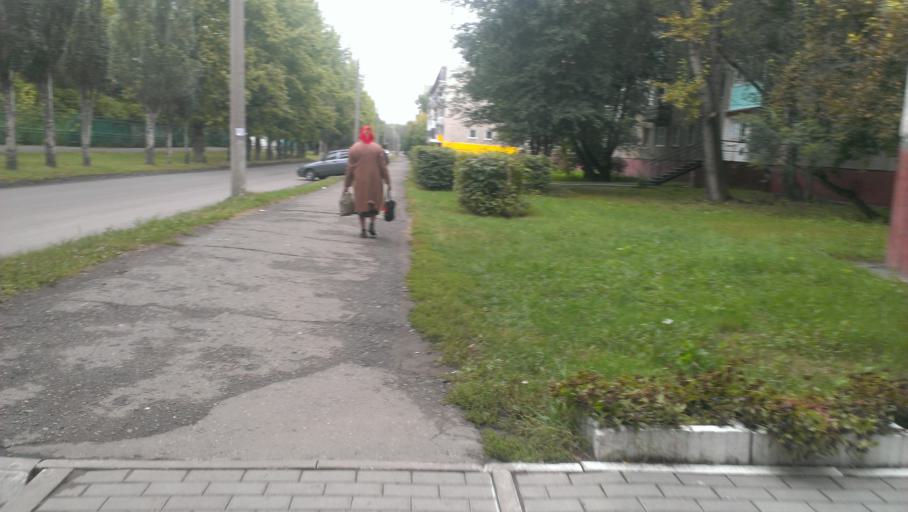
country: RU
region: Altai Krai
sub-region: Gorod Barnaulskiy
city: Barnaul
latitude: 53.3695
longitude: 83.6898
